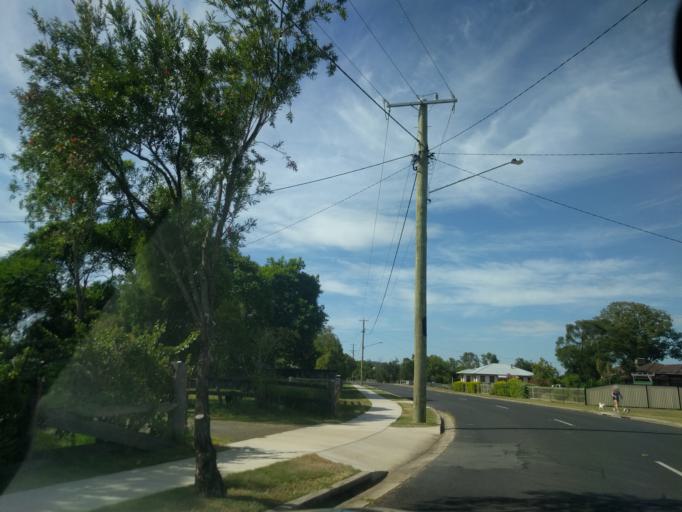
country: AU
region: Queensland
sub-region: Ipswich
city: Thagoona
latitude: -27.5694
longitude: 152.5971
